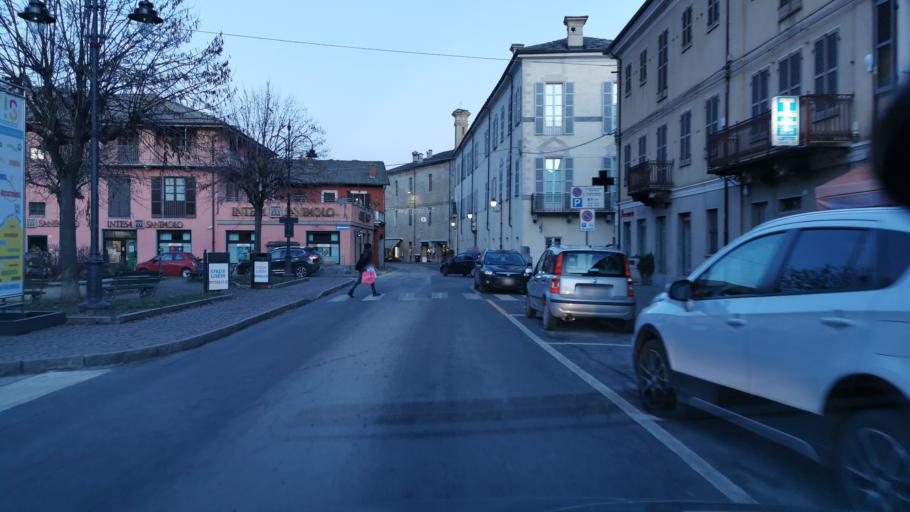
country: IT
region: Piedmont
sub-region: Provincia di Cuneo
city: Caraglio
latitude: 44.4180
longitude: 7.4299
